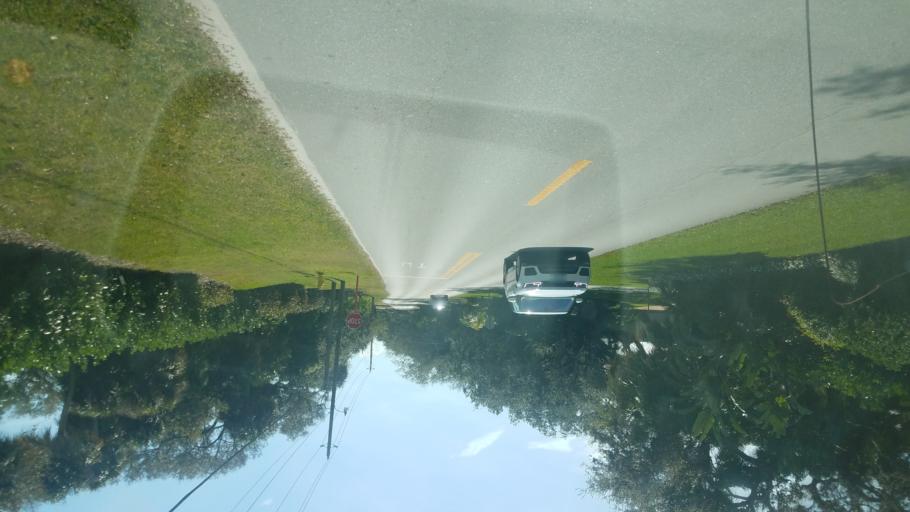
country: US
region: Florida
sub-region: Indian River County
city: Vero Beach
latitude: 27.6350
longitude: -80.3565
